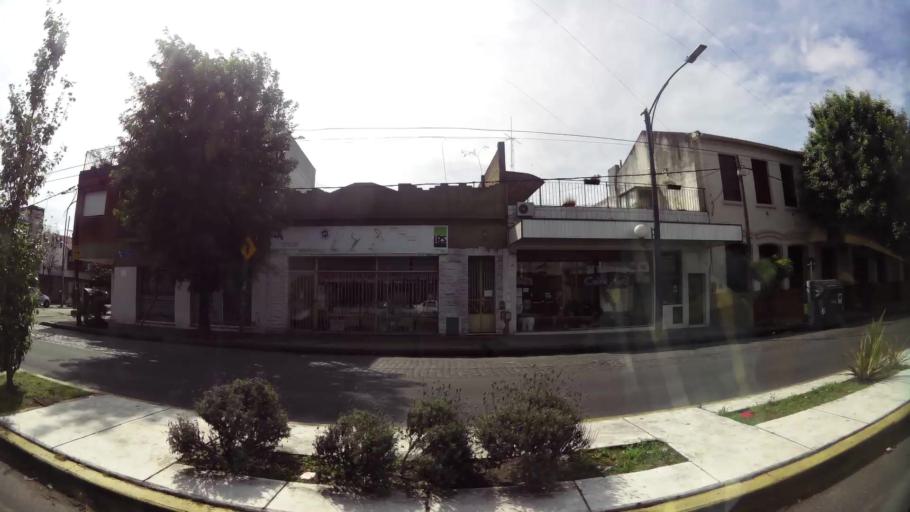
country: AR
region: Buenos Aires F.D.
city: Villa Lugano
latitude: -34.6683
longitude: -58.5071
